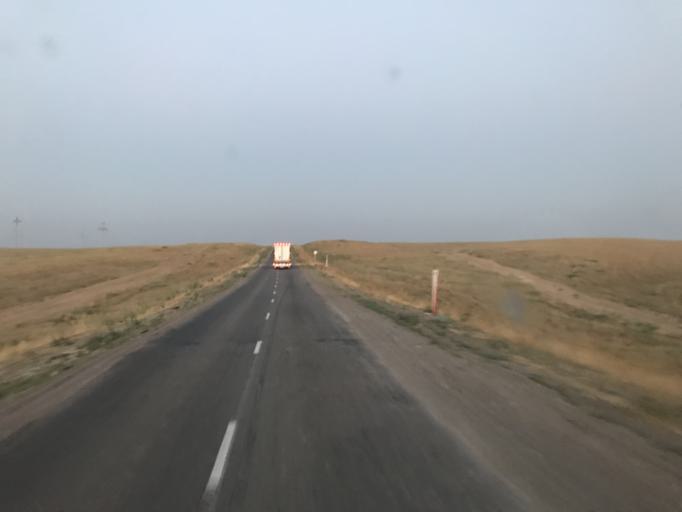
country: UZ
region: Toshkent
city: Chinoz
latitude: 41.1602
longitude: 68.6589
